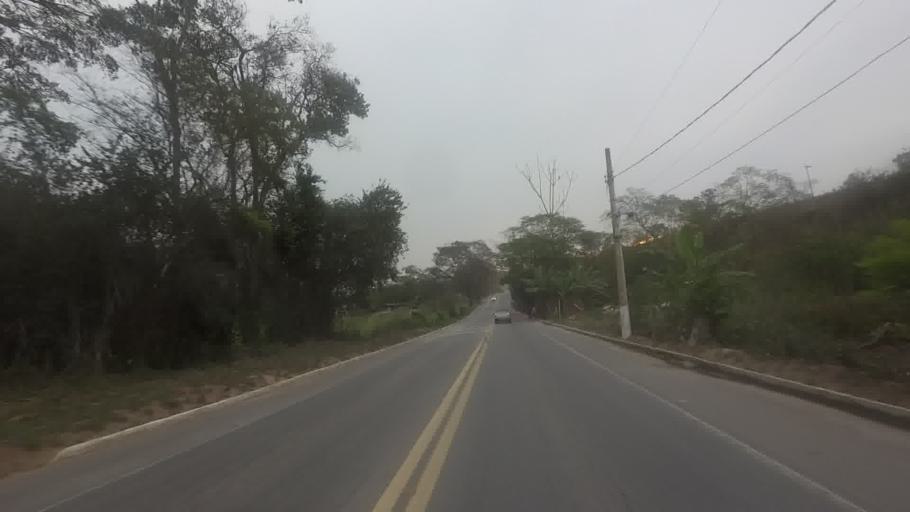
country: BR
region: Minas Gerais
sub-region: Recreio
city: Recreio
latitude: -21.6548
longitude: -42.3581
